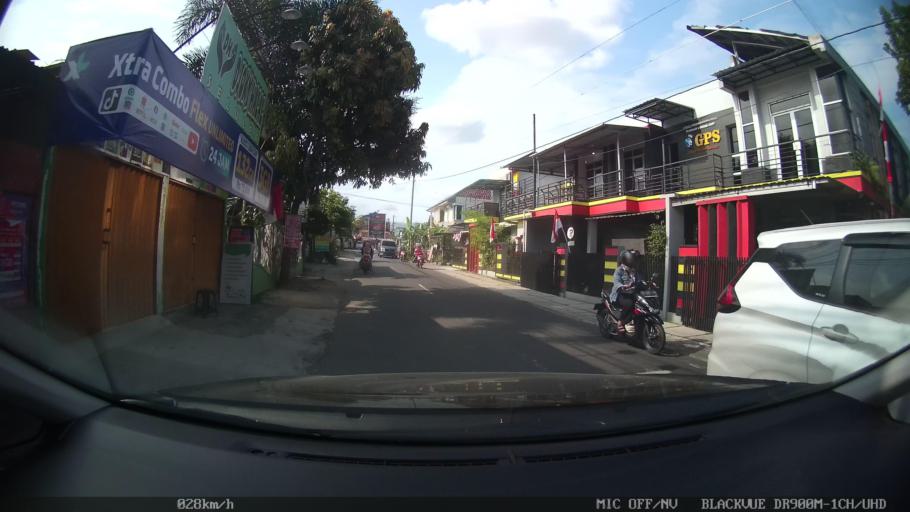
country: ID
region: Daerah Istimewa Yogyakarta
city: Depok
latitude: -7.7536
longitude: 110.4416
